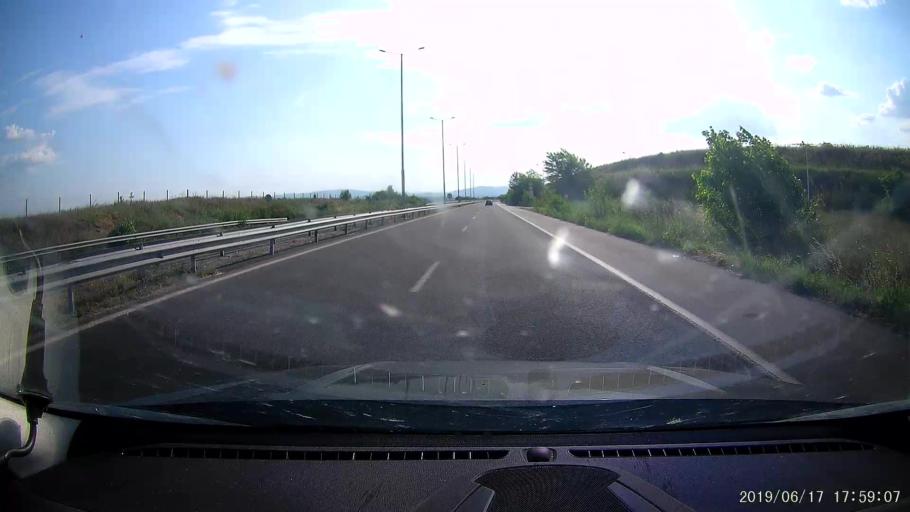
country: BG
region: Khaskovo
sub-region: Obshtina Svilengrad
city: Svilengrad
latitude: 41.7250
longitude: 26.3057
